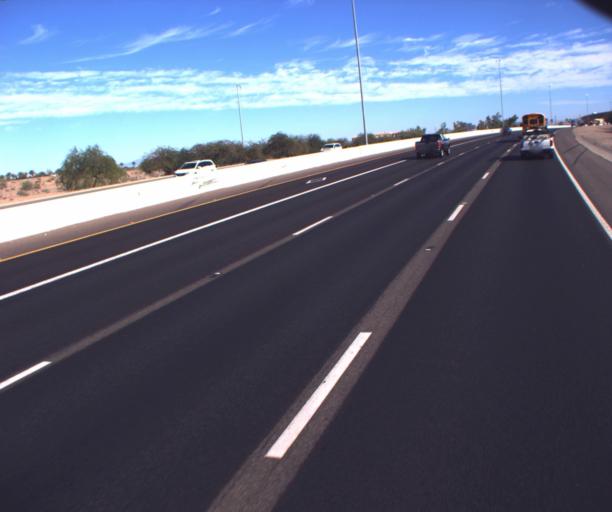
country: US
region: Arizona
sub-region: Maricopa County
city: Sun City
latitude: 33.5965
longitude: -112.2590
